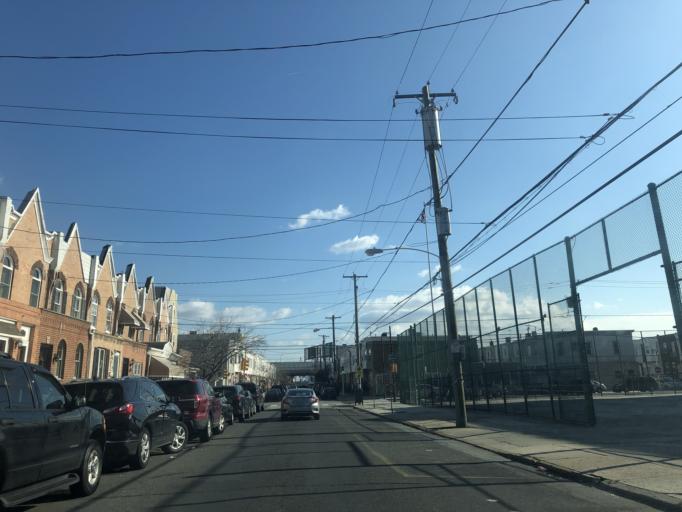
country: US
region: New Jersey
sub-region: Camden County
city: Camden
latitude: 39.9194
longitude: -75.1513
